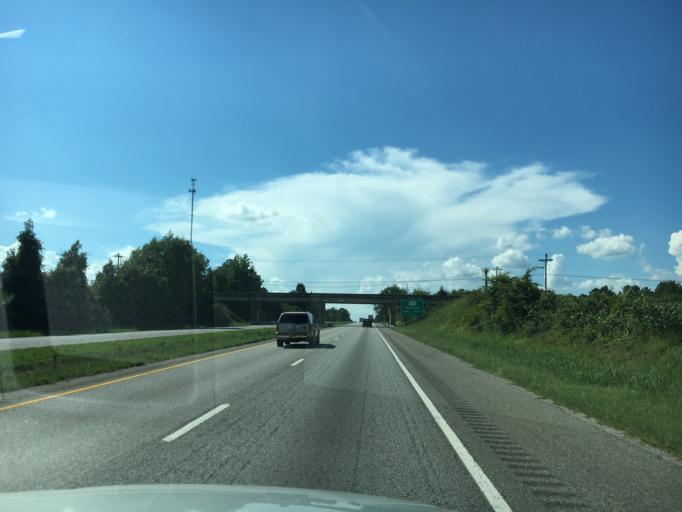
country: US
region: South Carolina
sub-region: Spartanburg County
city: Woodruff
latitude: 34.6158
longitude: -82.0817
